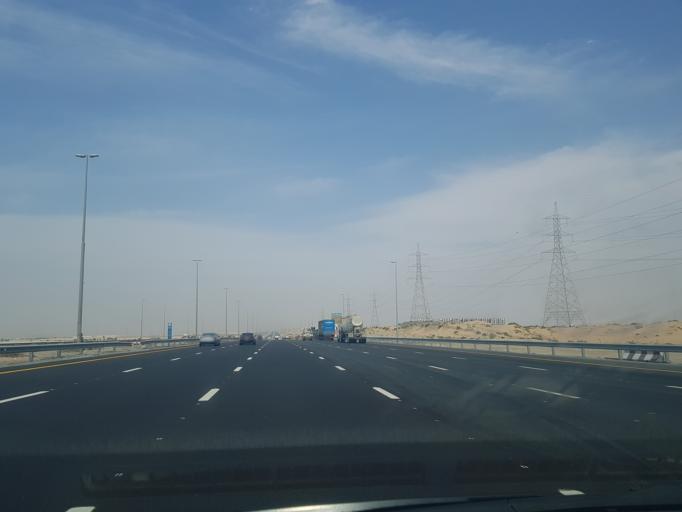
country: AE
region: Ash Shariqah
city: Sharjah
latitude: 25.2541
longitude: 55.5737
